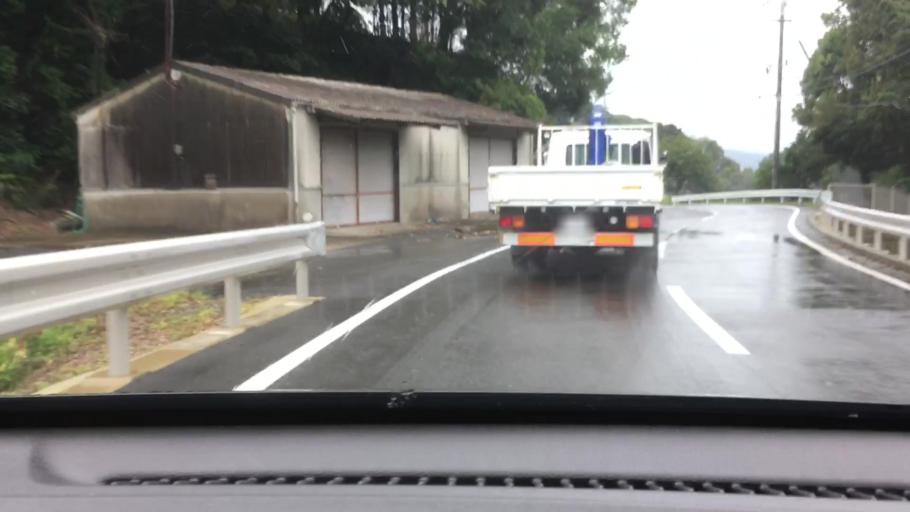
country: JP
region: Nagasaki
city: Togitsu
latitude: 32.8678
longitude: 129.7683
